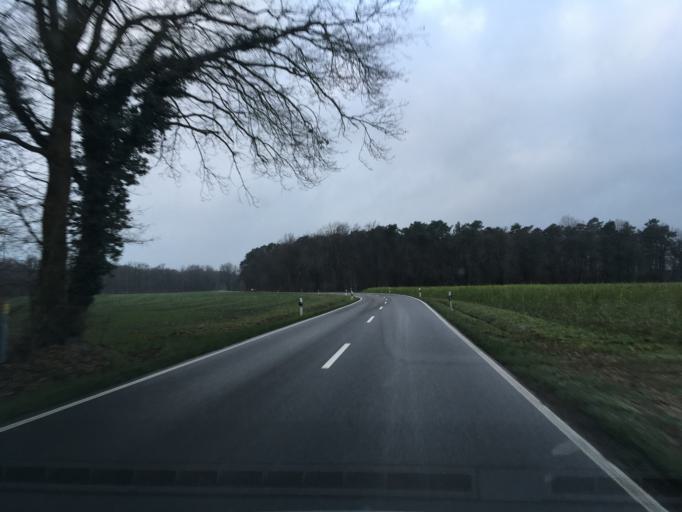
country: DE
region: North Rhine-Westphalia
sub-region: Regierungsbezirk Munster
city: Heek
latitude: 52.1644
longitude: 7.1216
